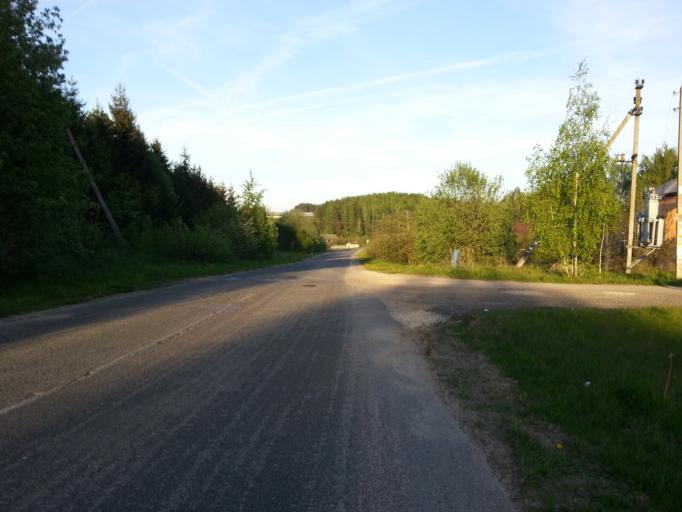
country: BY
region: Minsk
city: Slabada
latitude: 54.0444
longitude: 27.8688
